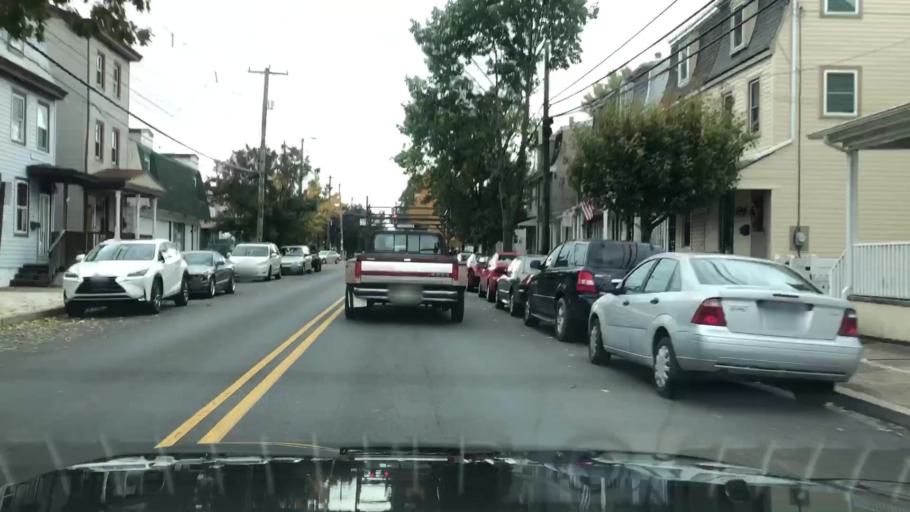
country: US
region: Pennsylvania
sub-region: Bucks County
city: Bristol
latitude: 40.1003
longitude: -74.8624
